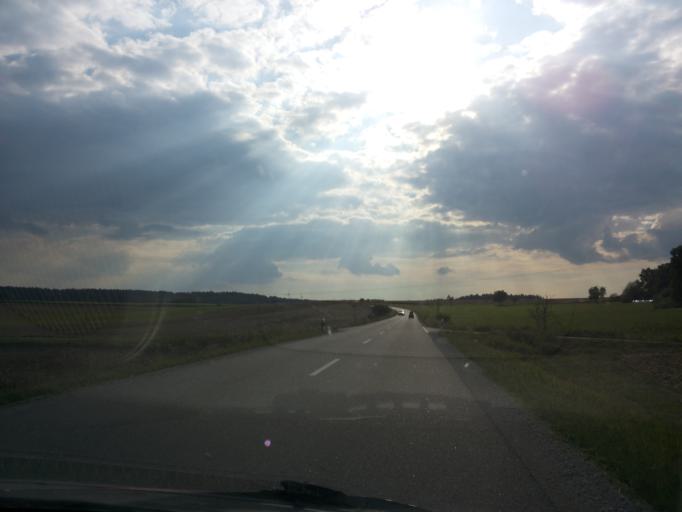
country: DE
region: Bavaria
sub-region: Upper Palatinate
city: Dietfurt
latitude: 48.9714
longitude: 11.5600
